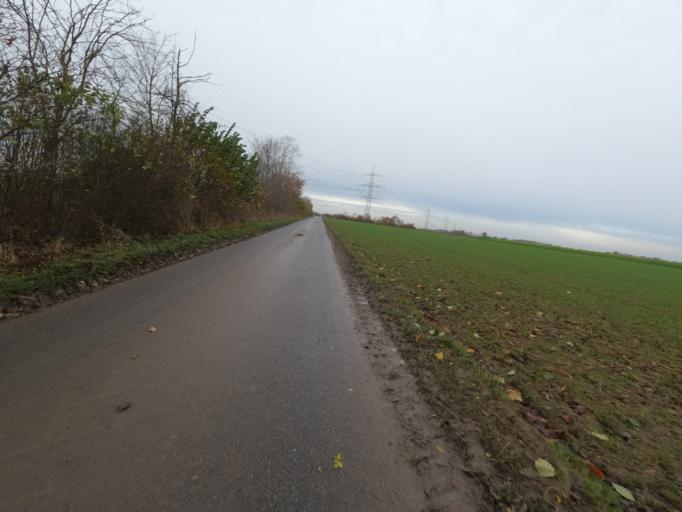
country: DE
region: North Rhine-Westphalia
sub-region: Regierungsbezirk Koln
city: Heinsberg
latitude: 51.0351
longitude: 6.1144
